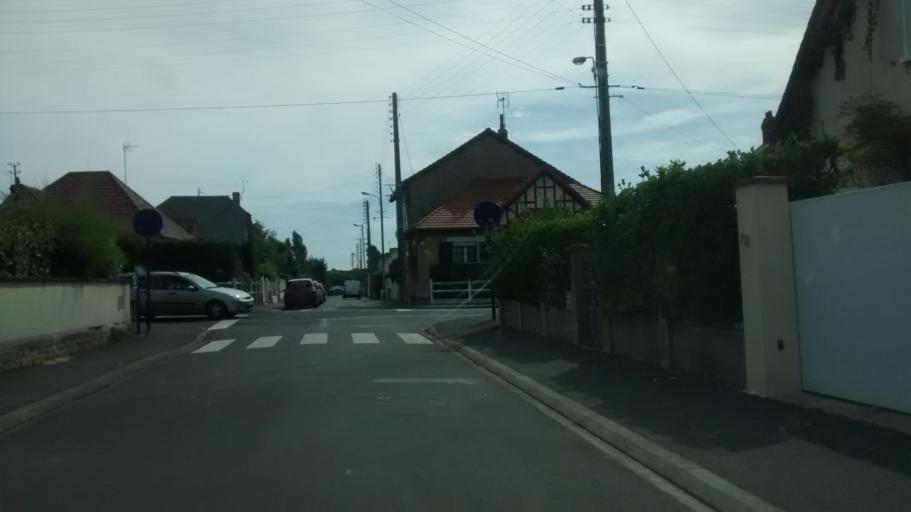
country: FR
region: Lower Normandy
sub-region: Departement du Calvados
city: Ouistreham
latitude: 49.2885
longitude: -0.2671
